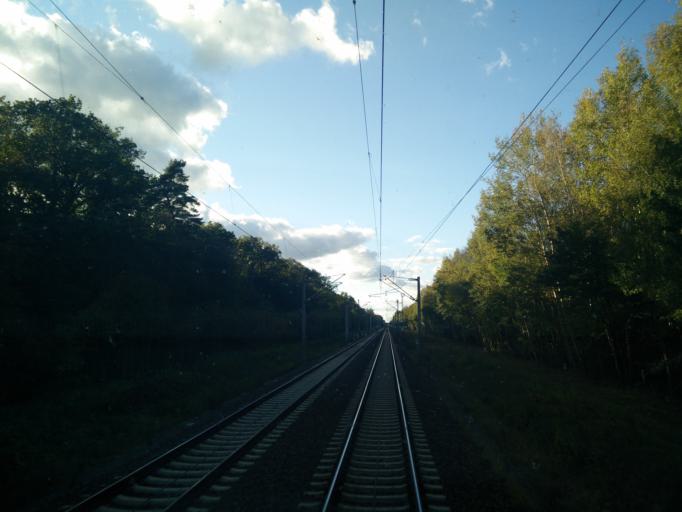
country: DE
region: Brandenburg
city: Brieselang
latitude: 52.5736
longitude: 13.0362
